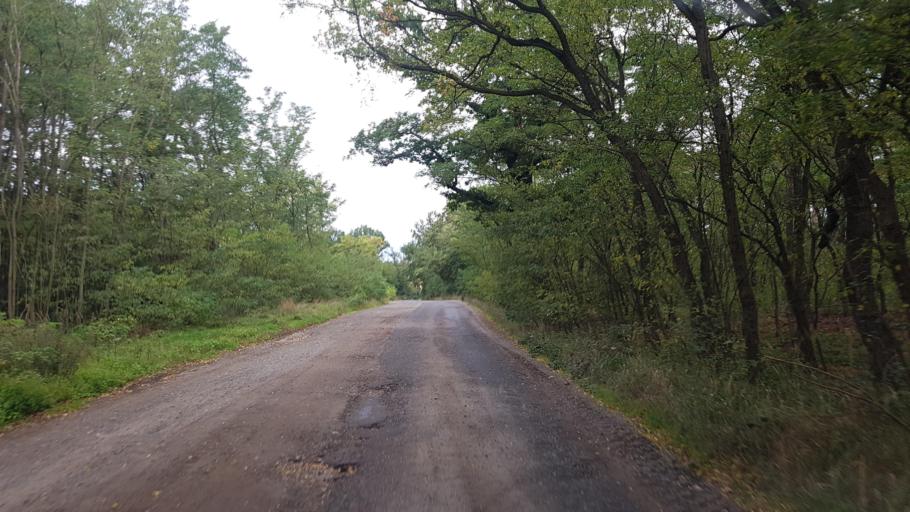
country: DE
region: Brandenburg
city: Kasel-Golzig
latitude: 51.9368
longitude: 13.7440
